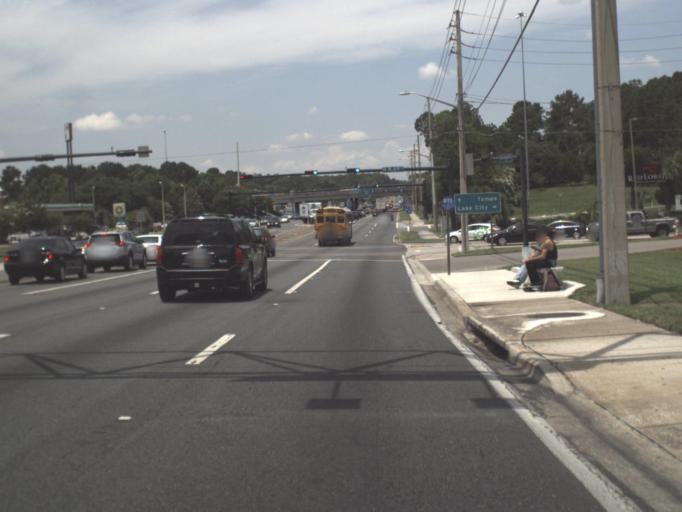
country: US
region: Florida
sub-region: Alachua County
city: Gainesville
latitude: 29.6598
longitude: -82.4157
